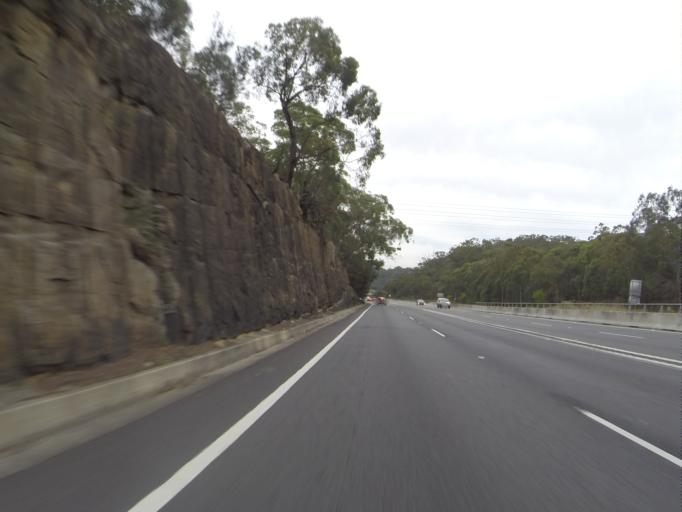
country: AU
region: New South Wales
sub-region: Hurstville
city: Lugarno
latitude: -33.9825
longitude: 151.0286
